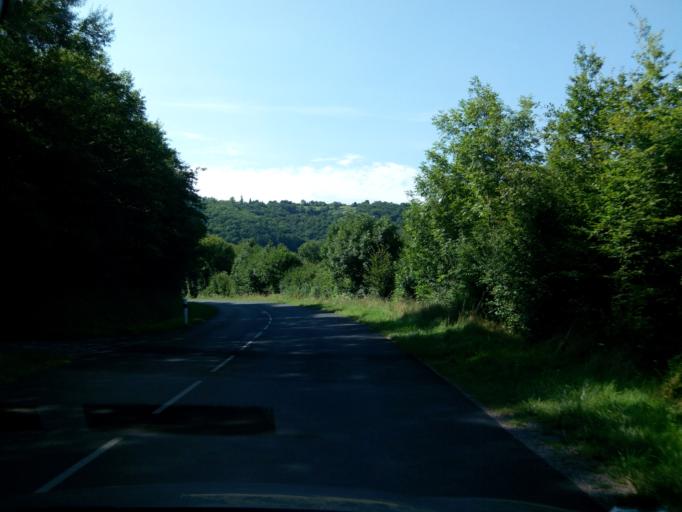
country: FR
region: Limousin
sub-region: Departement de la Correze
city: Beynat
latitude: 45.1297
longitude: 1.6822
